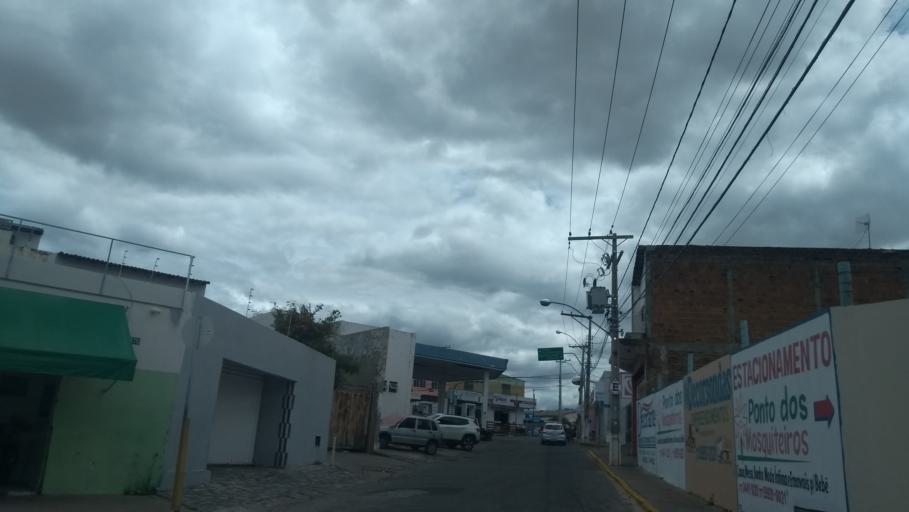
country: BR
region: Bahia
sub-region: Brumado
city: Brumado
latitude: -14.2092
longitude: -41.6700
